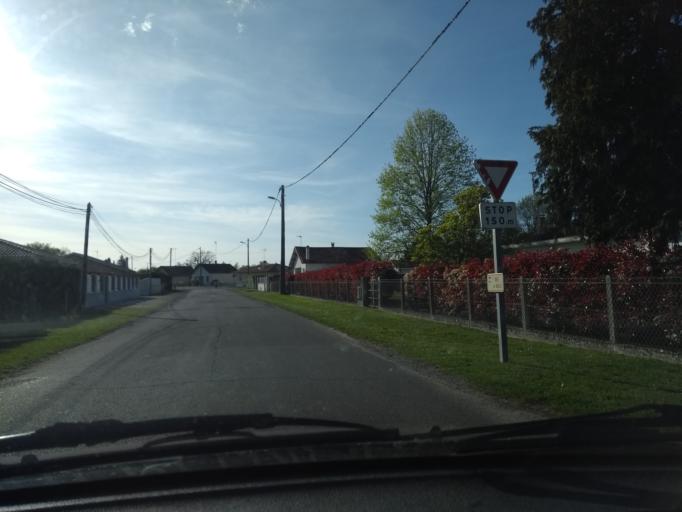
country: FR
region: Aquitaine
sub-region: Departement des Landes
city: Parentis-en-Born
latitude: 44.3540
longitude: -1.0703
